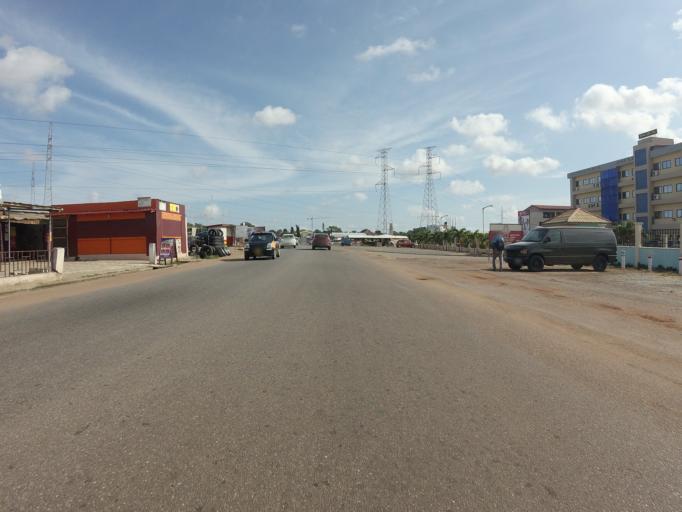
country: GH
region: Greater Accra
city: Medina Estates
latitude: 5.6436
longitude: -0.1700
